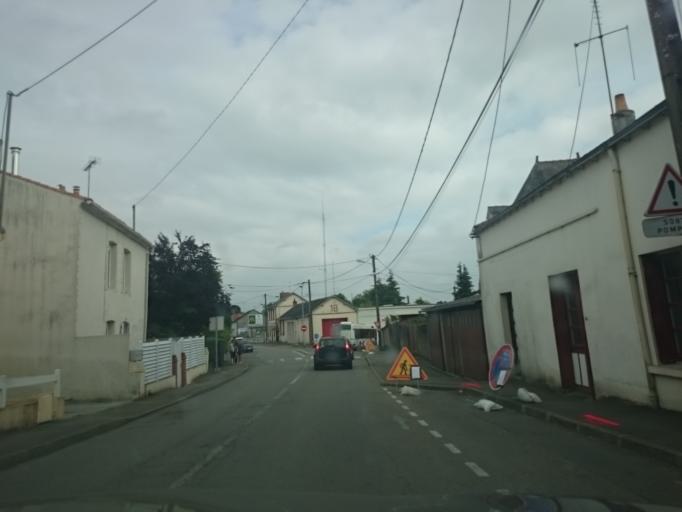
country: FR
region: Pays de la Loire
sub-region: Departement de la Loire-Atlantique
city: La Montagne
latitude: 47.1892
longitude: -1.6909
